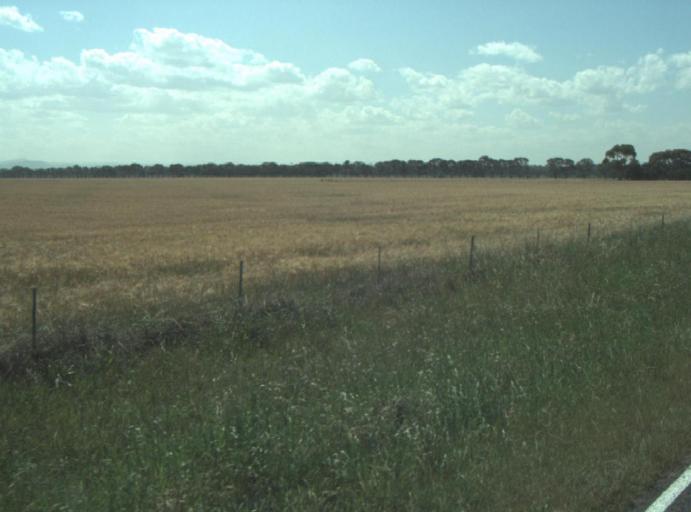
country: AU
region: Victoria
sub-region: Greater Geelong
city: Lara
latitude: -37.9838
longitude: 144.4033
